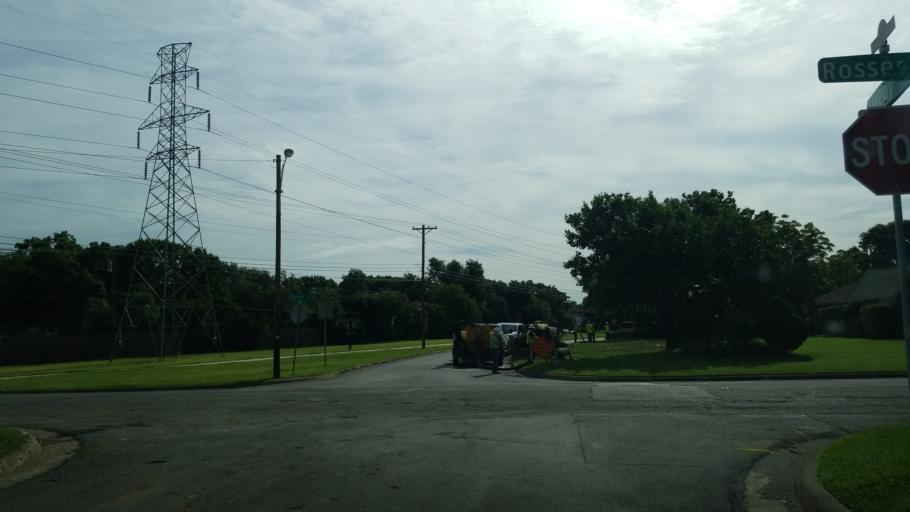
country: US
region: Texas
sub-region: Dallas County
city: Farmers Branch
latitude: 32.8994
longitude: -96.8475
